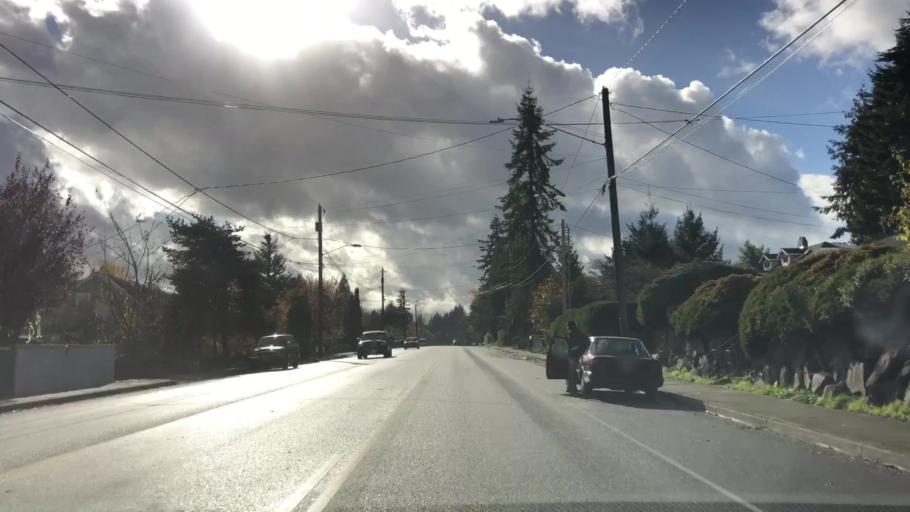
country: US
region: Washington
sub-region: Snohomish County
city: Everett
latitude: 47.9395
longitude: -122.2081
